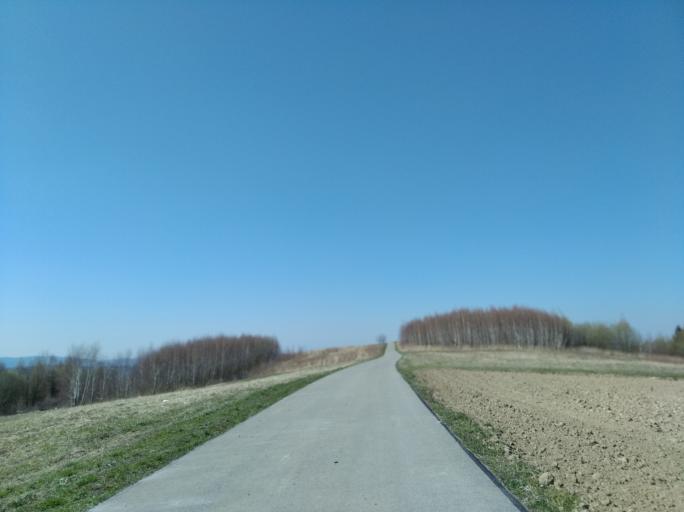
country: PL
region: Subcarpathian Voivodeship
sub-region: Powiat strzyzowski
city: Strzyzow
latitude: 49.8637
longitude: 21.8438
